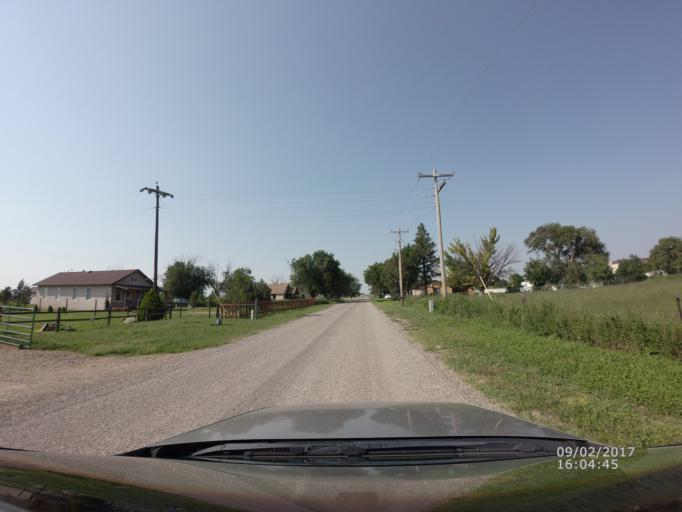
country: US
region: New Mexico
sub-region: Curry County
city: Clovis
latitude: 34.4453
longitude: -103.1996
